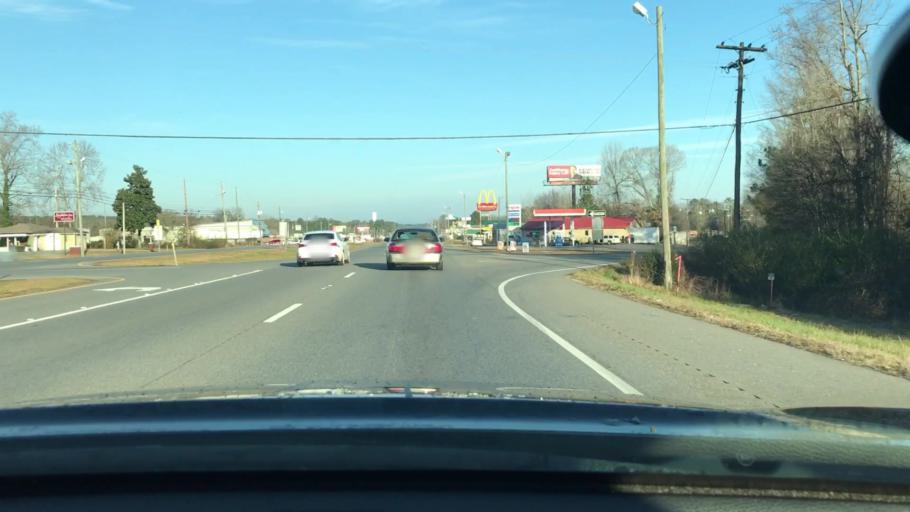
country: US
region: Alabama
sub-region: Talladega County
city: Childersburg
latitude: 33.2622
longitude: -86.3489
